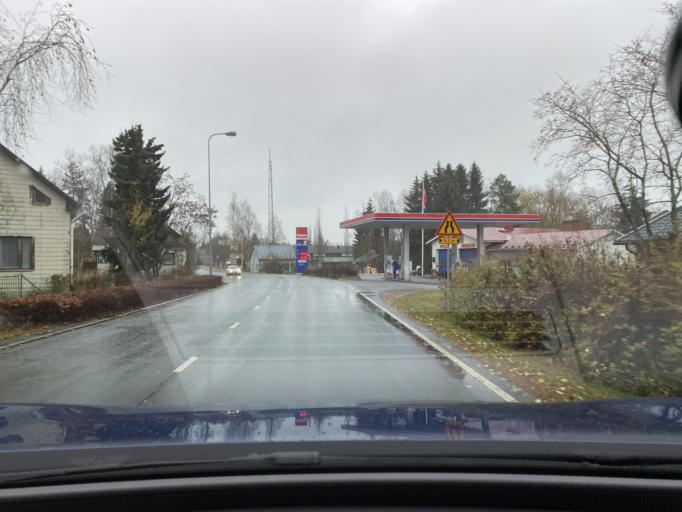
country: FI
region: Varsinais-Suomi
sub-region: Loimaa
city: Alastaro
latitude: 60.9487
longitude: 22.8649
